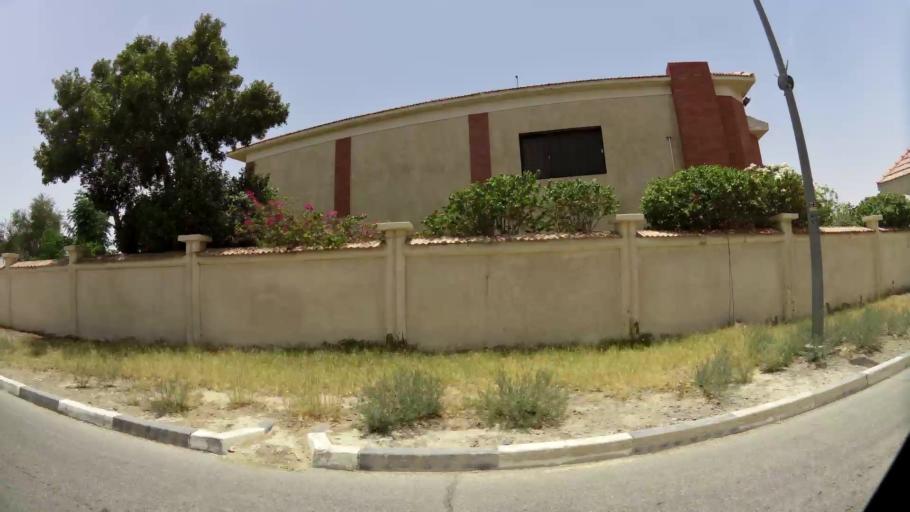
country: AE
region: Abu Dhabi
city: Al Ain
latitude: 24.2222
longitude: 55.7281
